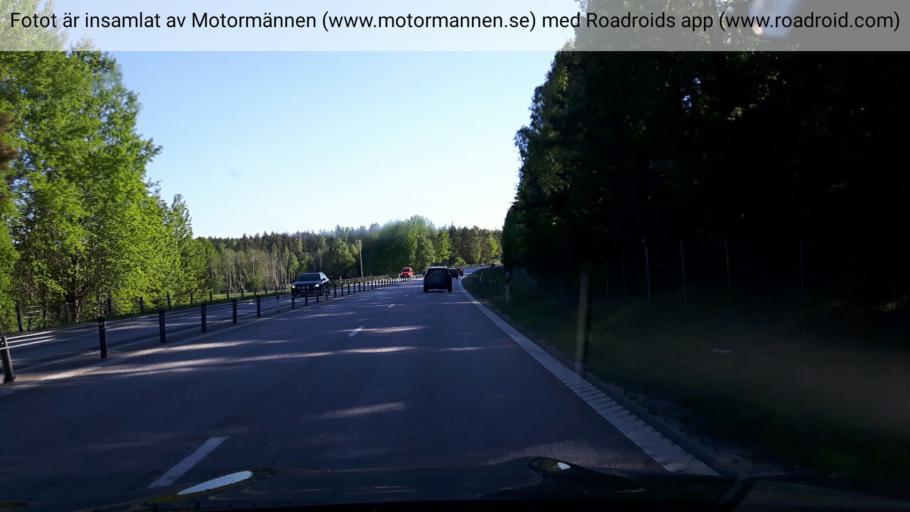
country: SE
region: Stockholm
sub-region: Osterakers Kommun
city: Akersberga
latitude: 59.5499
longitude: 18.2275
